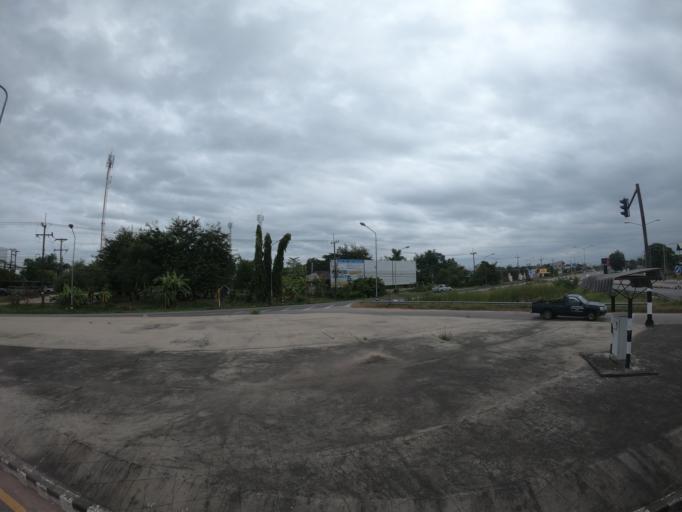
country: TH
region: Maha Sarakham
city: Maha Sarakham
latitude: 16.1647
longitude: 103.3354
